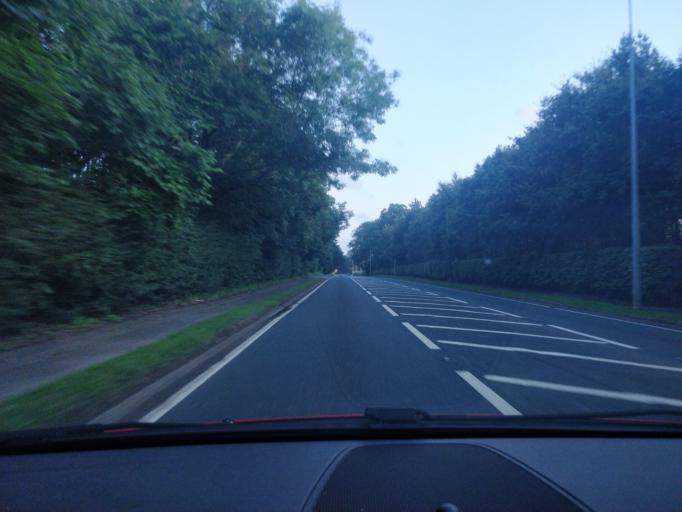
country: GB
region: England
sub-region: Lancashire
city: Tarleton
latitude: 53.6820
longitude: -2.8166
